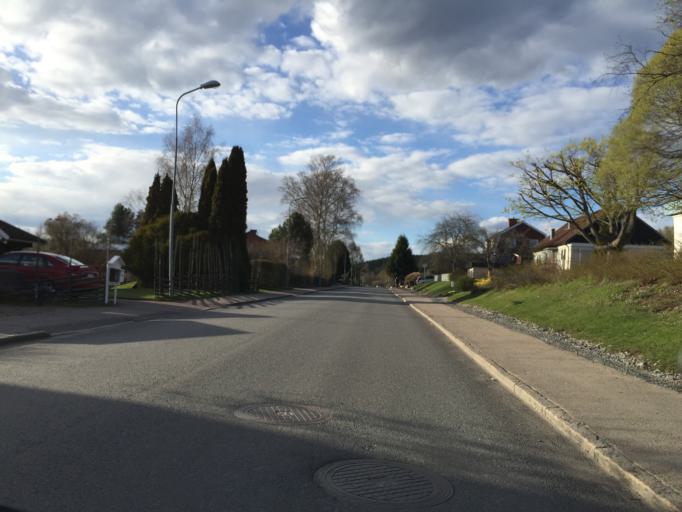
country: SE
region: Dalarna
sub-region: Ludvika Kommun
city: Ludvika
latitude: 60.1210
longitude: 15.1930
